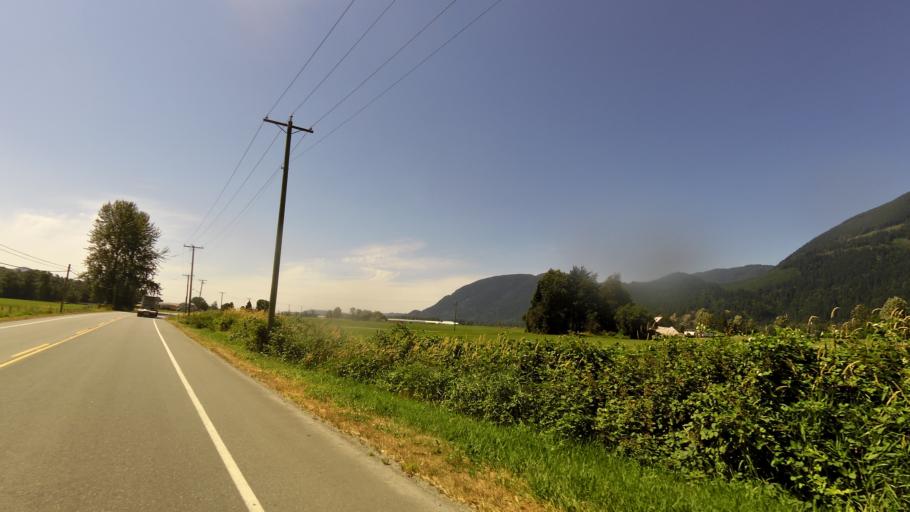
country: CA
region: British Columbia
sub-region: Fraser Valley Regional District
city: Chilliwack
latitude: 49.1702
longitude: -122.0928
